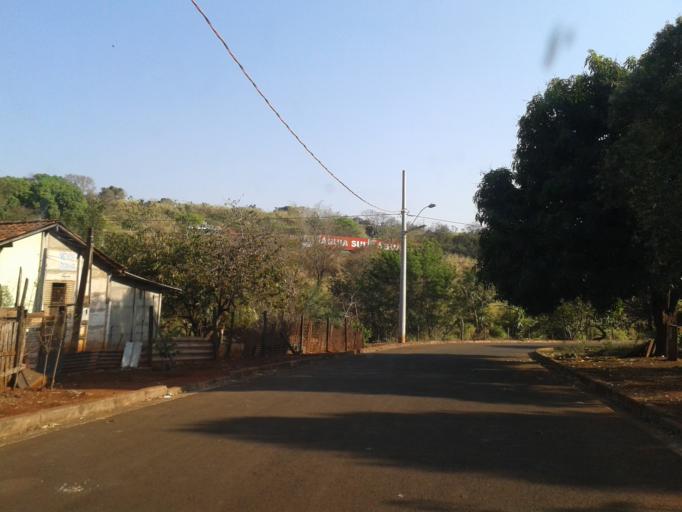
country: BR
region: Minas Gerais
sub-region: Ituiutaba
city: Ituiutaba
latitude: -18.9633
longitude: -49.4735
